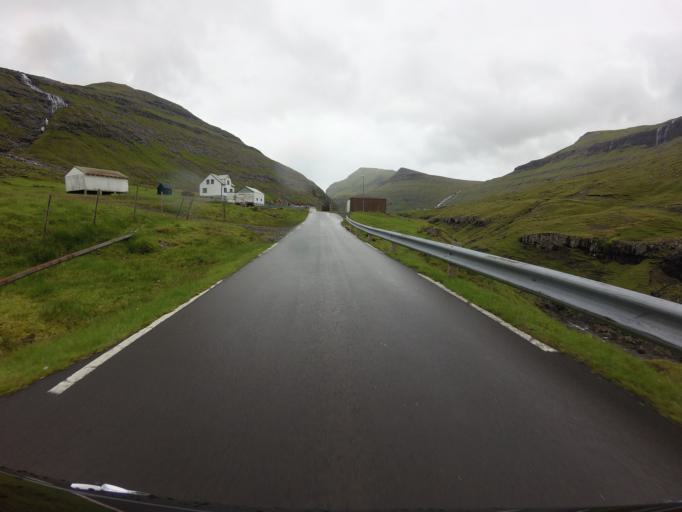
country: FO
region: Streymoy
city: Vestmanna
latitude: 62.2423
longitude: -7.1666
